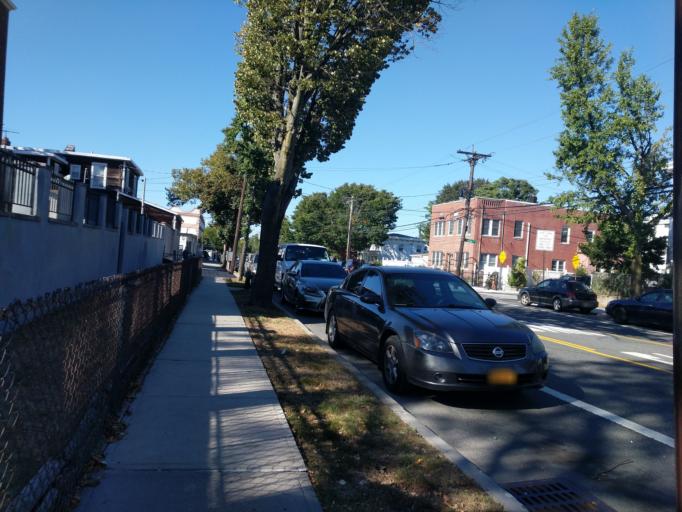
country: US
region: New York
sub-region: Nassau County
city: Kings Point
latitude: 40.8401
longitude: -73.7839
